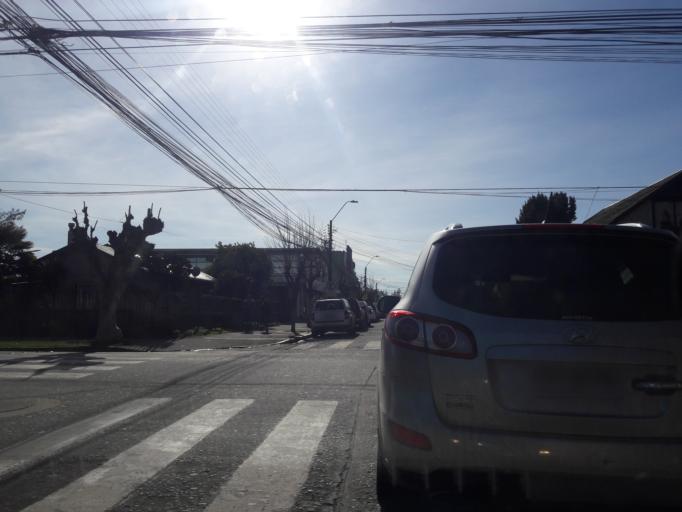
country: CL
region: Biobio
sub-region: Provincia de Biobio
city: Cabrero
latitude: -37.0357
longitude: -72.4032
